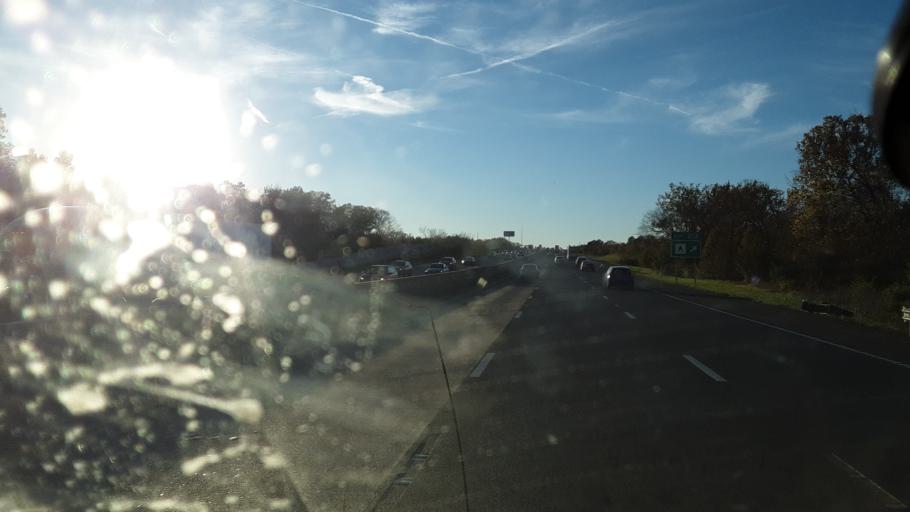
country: US
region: Missouri
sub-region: Saint Charles County
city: Lake Saint Louis
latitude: 38.8054
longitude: -90.8002
